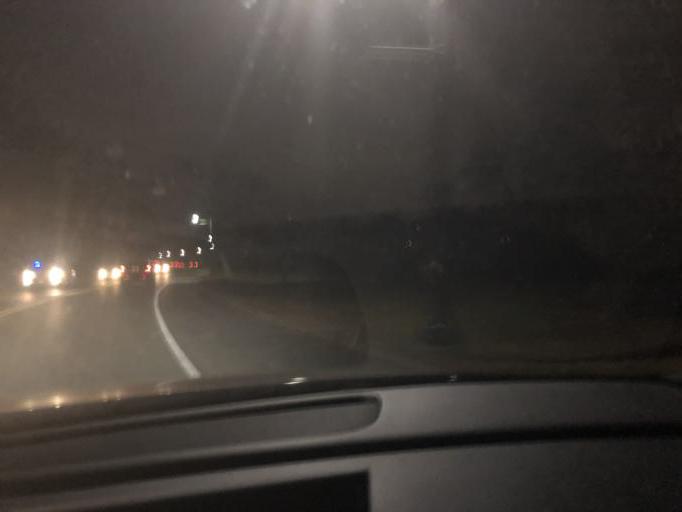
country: US
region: New Jersey
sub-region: Essex County
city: East Orange
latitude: 40.7611
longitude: -74.1830
